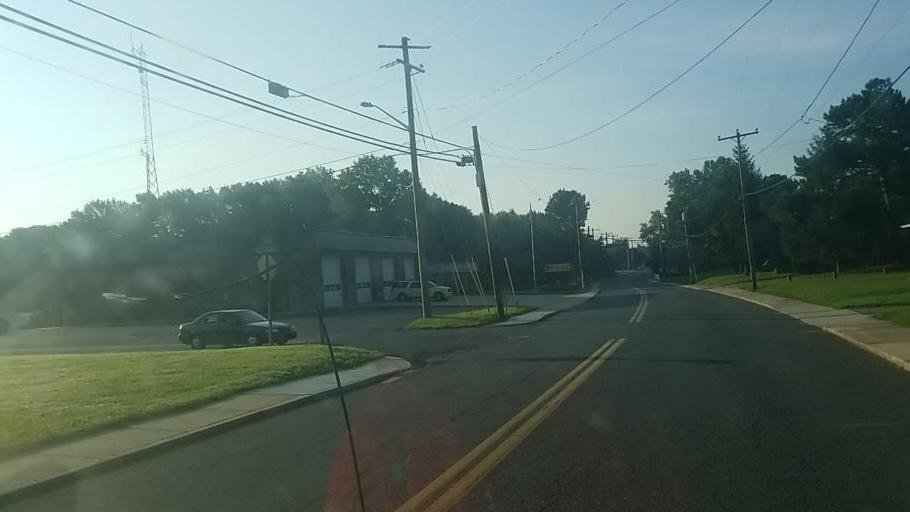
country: US
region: Delaware
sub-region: Sussex County
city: Selbyville
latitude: 38.4637
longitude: -75.2238
